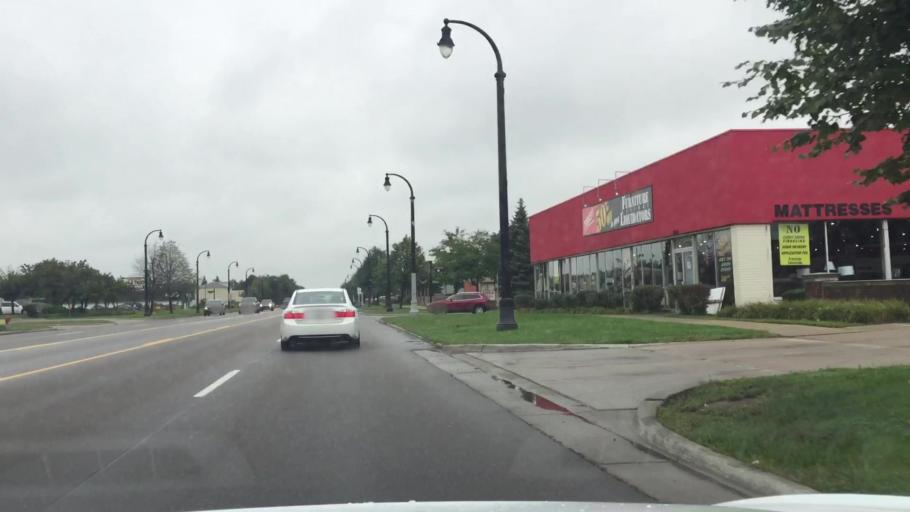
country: US
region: Michigan
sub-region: Wayne County
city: Livonia
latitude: 42.3692
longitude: -83.3294
